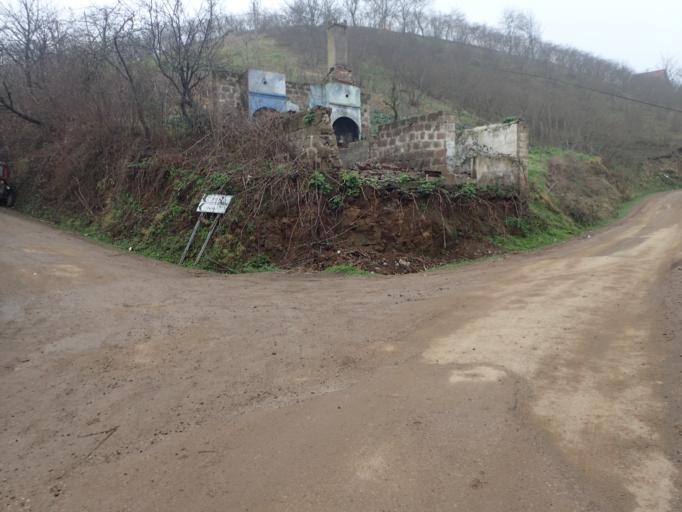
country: TR
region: Ordu
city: Camas
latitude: 40.9124
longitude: 37.5645
